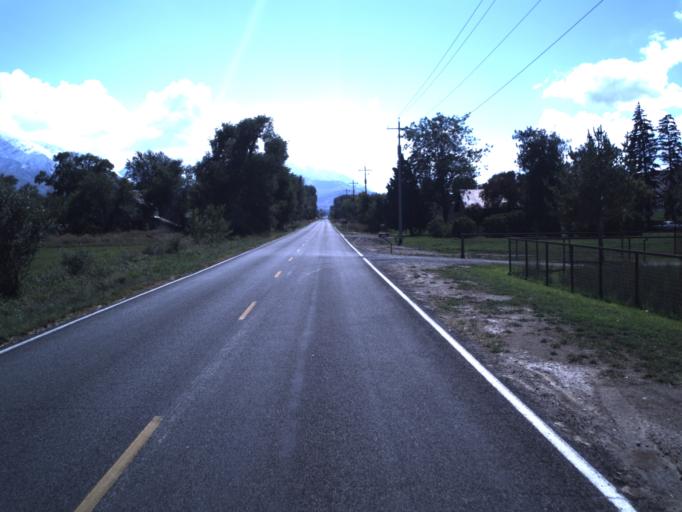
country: US
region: Utah
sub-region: Utah County
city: West Mountain
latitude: 40.0626
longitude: -111.7876
